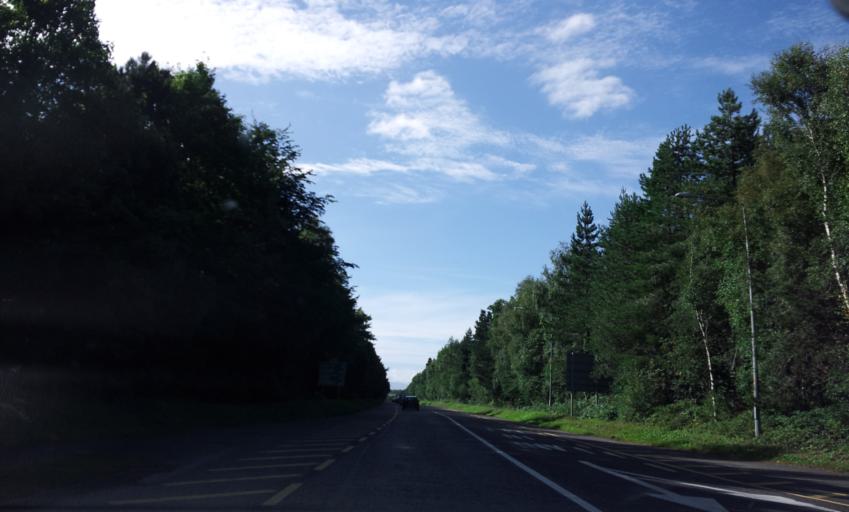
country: IE
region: Munster
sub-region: Ciarrai
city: Cill Airne
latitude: 52.0631
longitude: -9.4866
